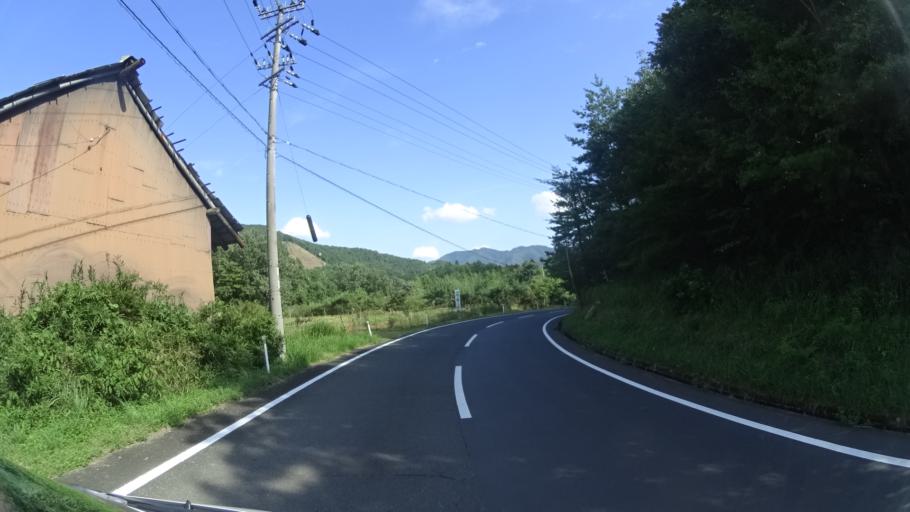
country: JP
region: Kyoto
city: Ayabe
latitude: 35.2877
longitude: 135.3300
